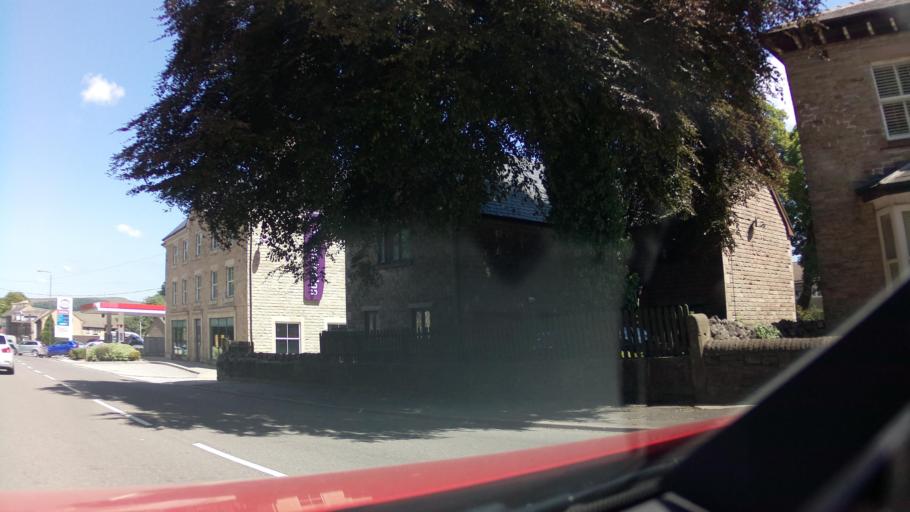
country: GB
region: England
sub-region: Derbyshire
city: Buxton
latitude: 53.2496
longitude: -1.9108
